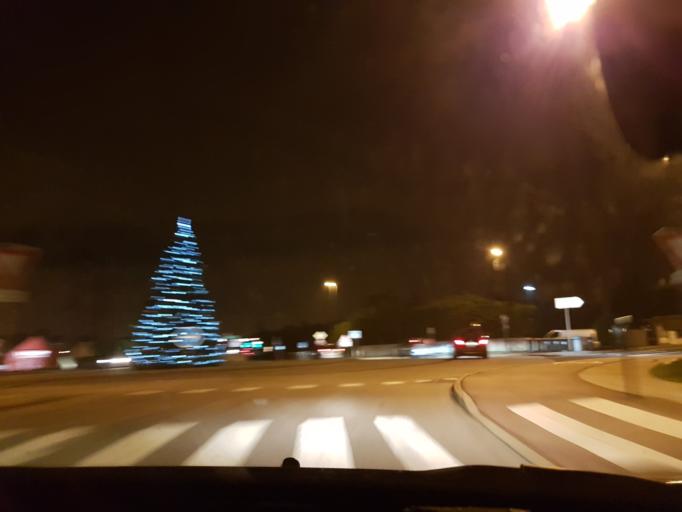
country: FR
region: Ile-de-France
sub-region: Departement des Yvelines
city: Chambourcy
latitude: 48.9042
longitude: 2.0542
